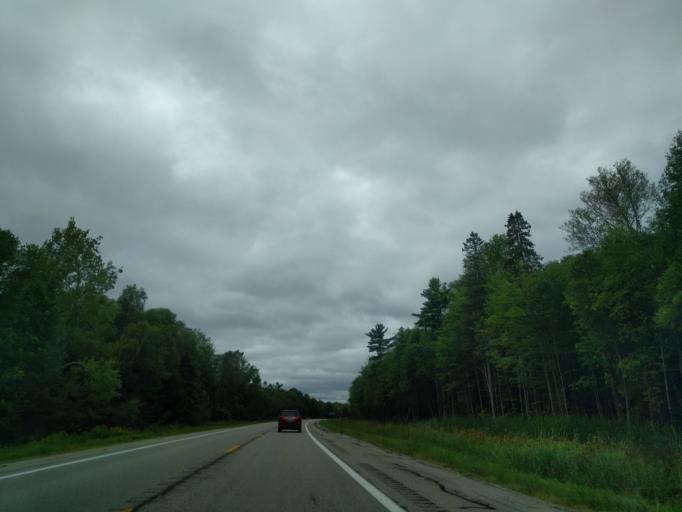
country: US
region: Michigan
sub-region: Delta County
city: Escanaba
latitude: 45.5881
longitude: -87.2383
